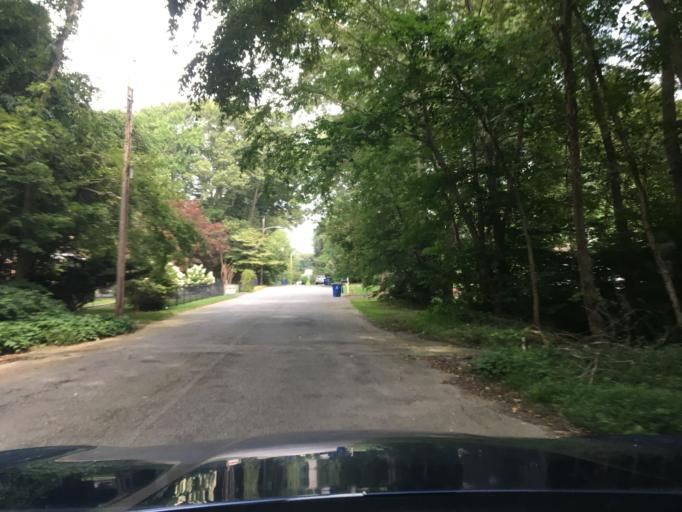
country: US
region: Rhode Island
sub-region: Kent County
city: East Greenwich
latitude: 41.6497
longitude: -71.4776
